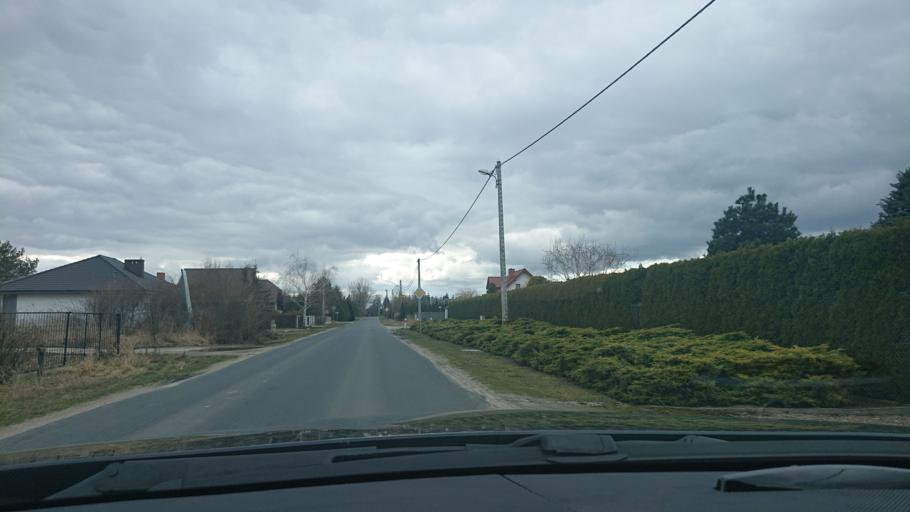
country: PL
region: Greater Poland Voivodeship
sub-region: Powiat gnieznienski
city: Gniezno
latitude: 52.5790
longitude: 17.6356
